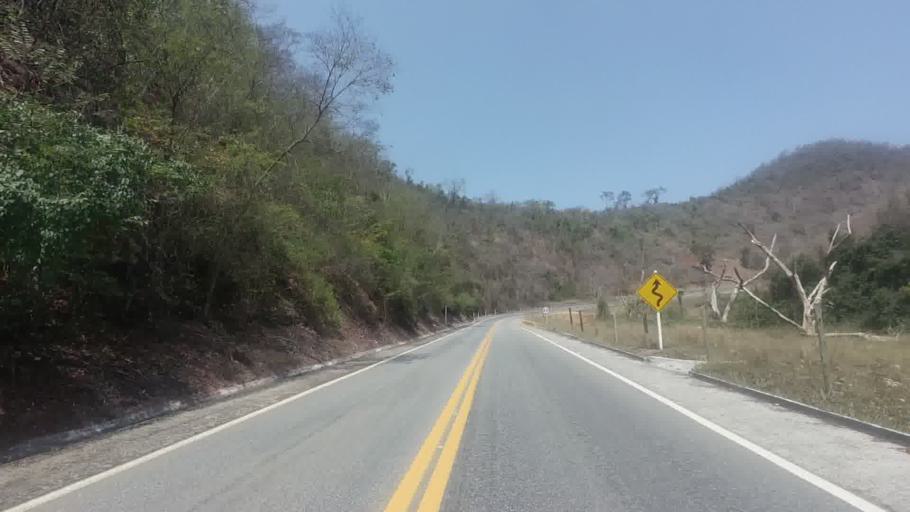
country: BR
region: Espirito Santo
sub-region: Cachoeiro De Itapemirim
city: Cachoeiro de Itapemirim
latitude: -20.8274
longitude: -41.2190
